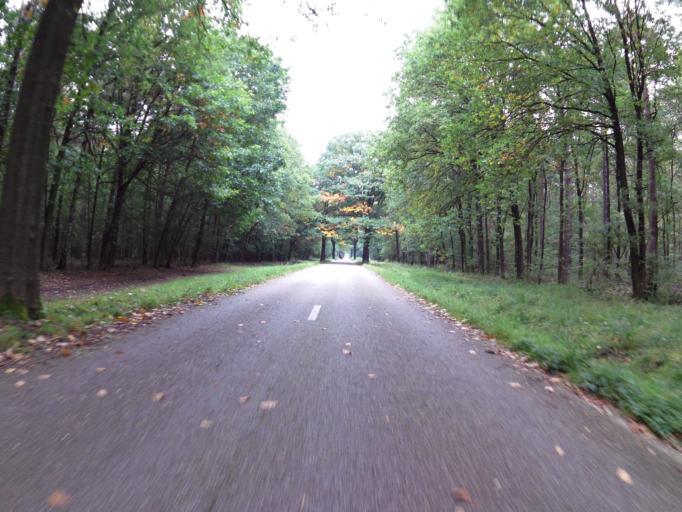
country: BE
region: Flanders
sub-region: Provincie Limburg
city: As
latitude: 50.9821
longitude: 5.5705
